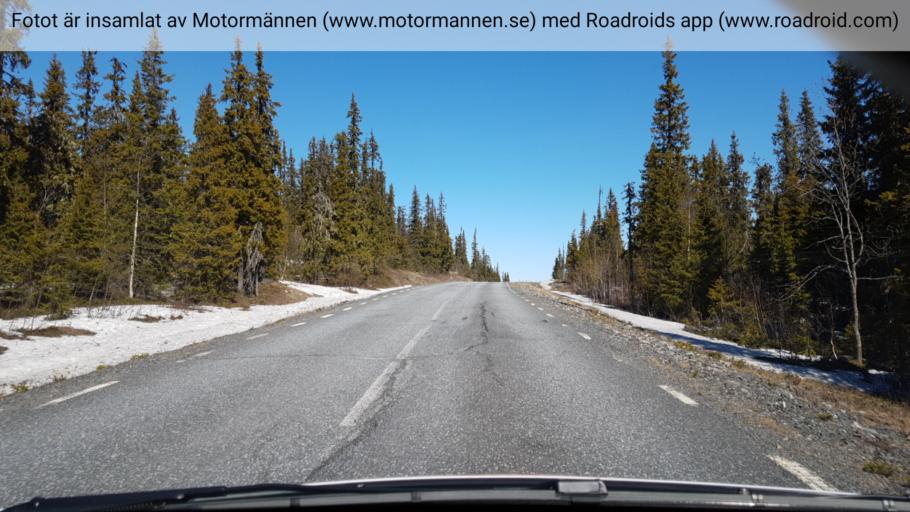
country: SE
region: Vaesterbotten
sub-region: Vilhelmina Kommun
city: Sjoberg
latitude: 65.0948
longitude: 15.8704
